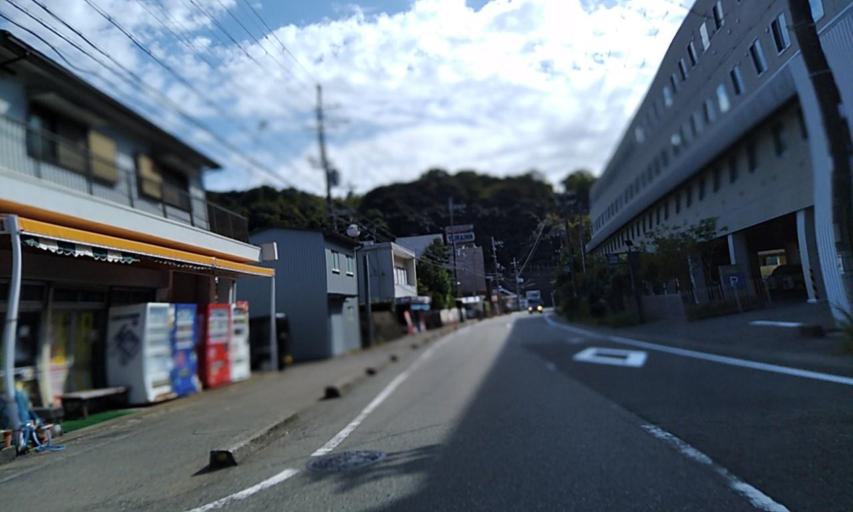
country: JP
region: Wakayama
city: Gobo
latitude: 33.9637
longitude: 135.1131
